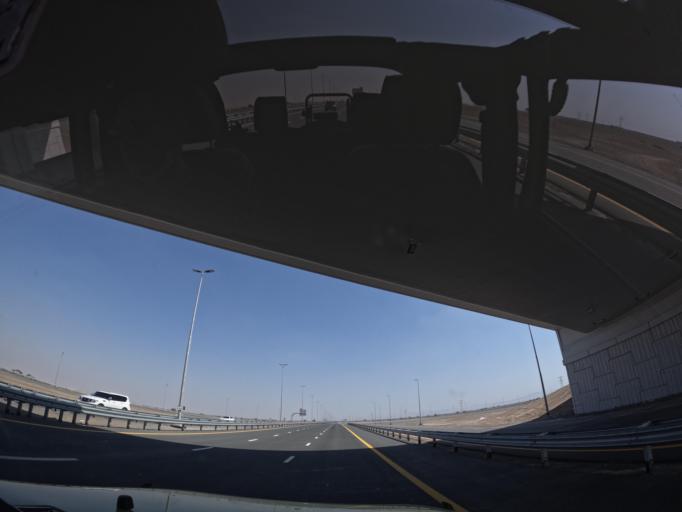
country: AE
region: Ash Shariqah
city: Adh Dhayd
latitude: 24.9306
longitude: 55.8155
